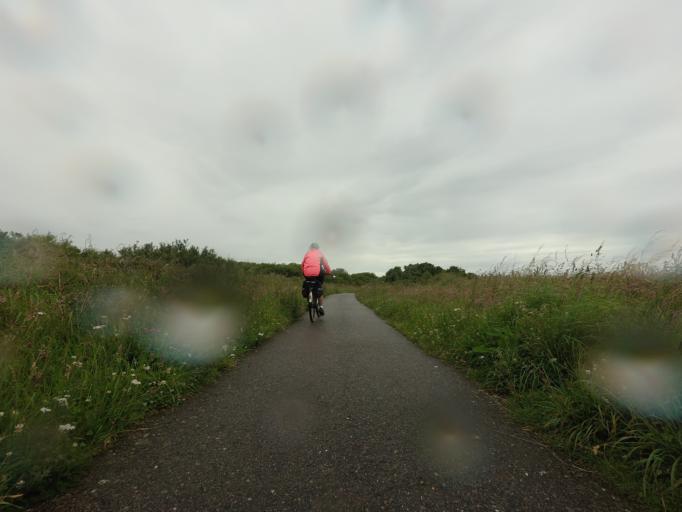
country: GB
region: Scotland
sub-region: Moray
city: Findochty
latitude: 57.6858
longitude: -2.9306
